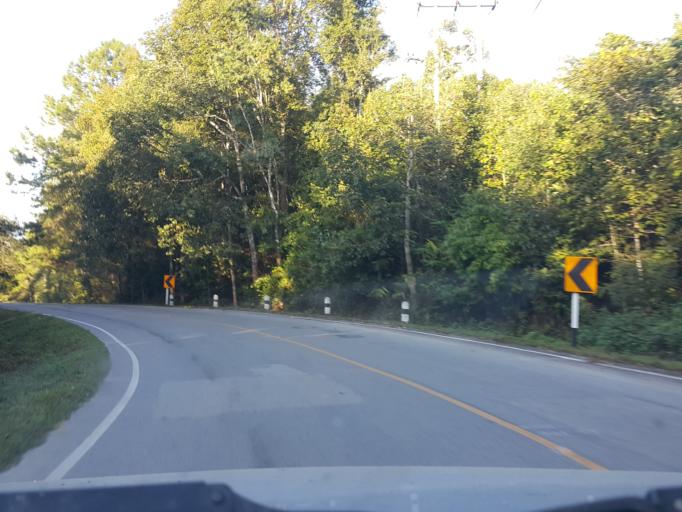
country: TH
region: Mae Hong Son
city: Mae Hi
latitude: 19.2715
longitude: 98.5986
